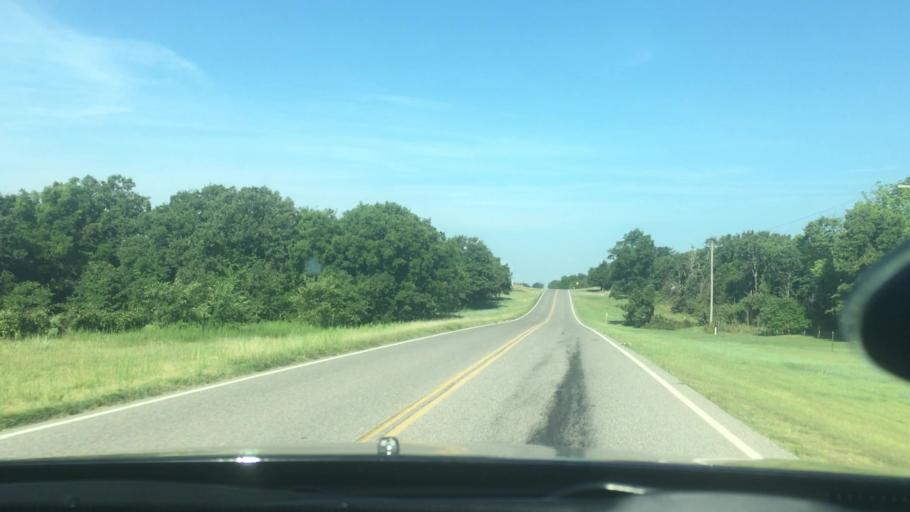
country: US
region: Oklahoma
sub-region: Garvin County
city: Pauls Valley
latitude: 34.6521
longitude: -97.3428
